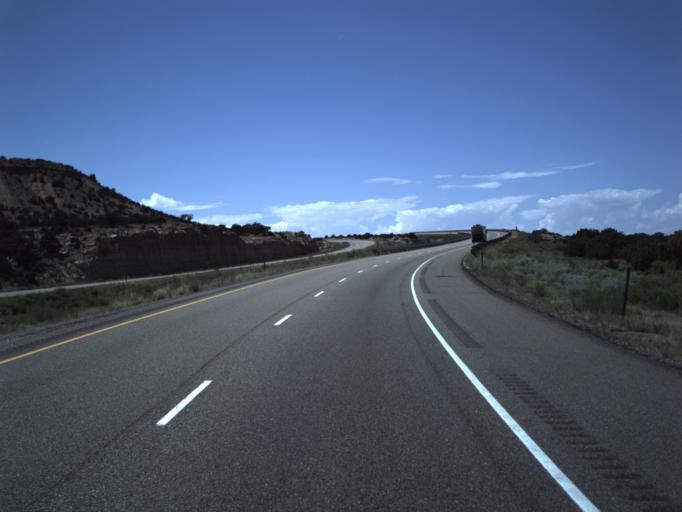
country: US
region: Utah
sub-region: Emery County
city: Castle Dale
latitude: 38.9137
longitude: -110.5090
